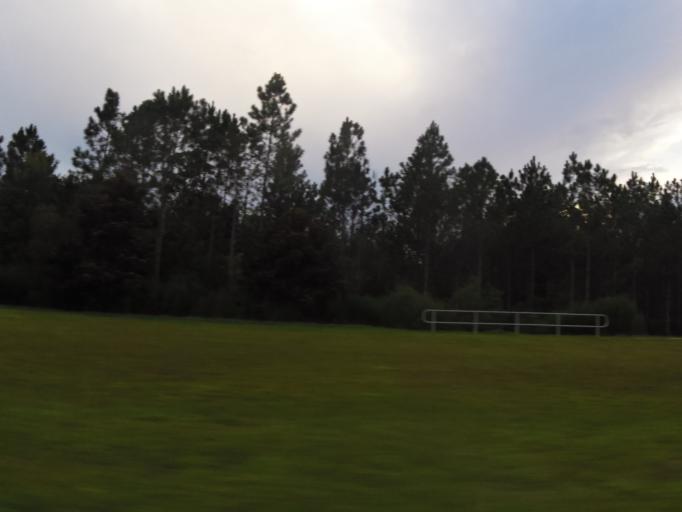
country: US
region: Florida
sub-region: Saint Johns County
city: Fruit Cove
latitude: 30.0872
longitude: -81.5785
